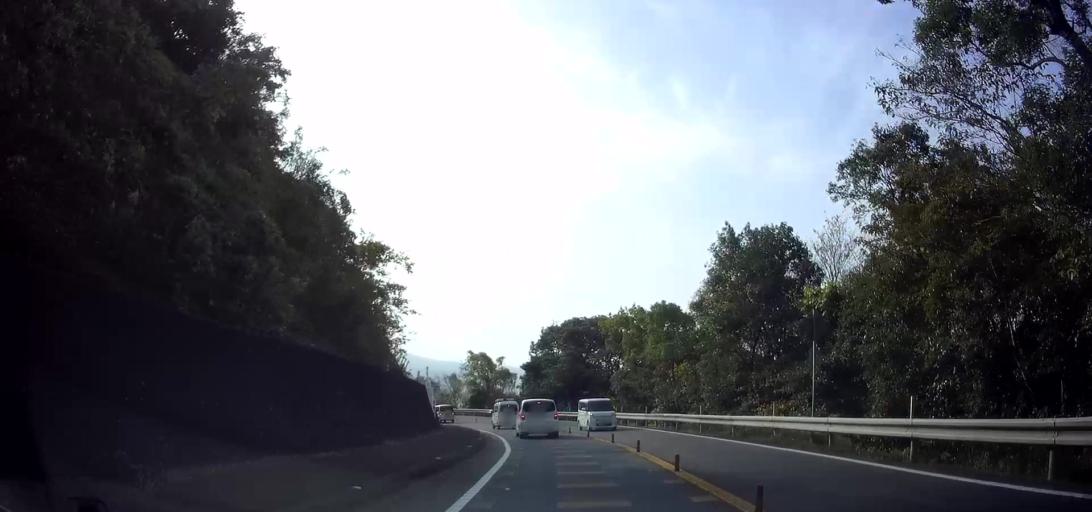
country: JP
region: Nagasaki
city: Shimabara
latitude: 32.7540
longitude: 130.2085
